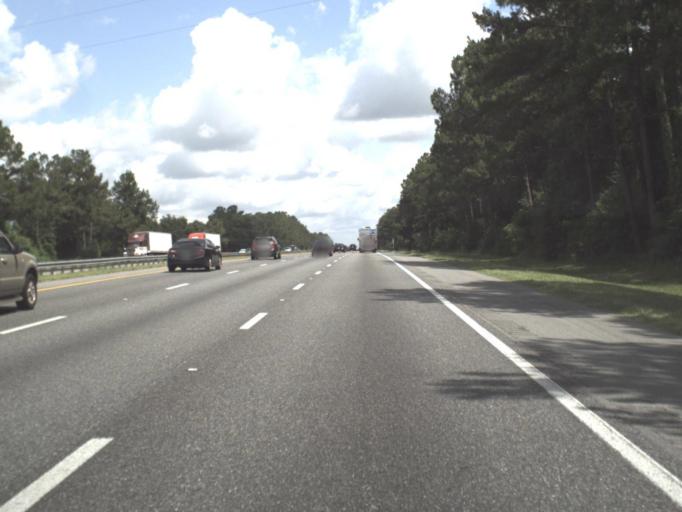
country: US
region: Florida
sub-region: Columbia County
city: Lake City
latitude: 30.0934
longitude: -82.6416
